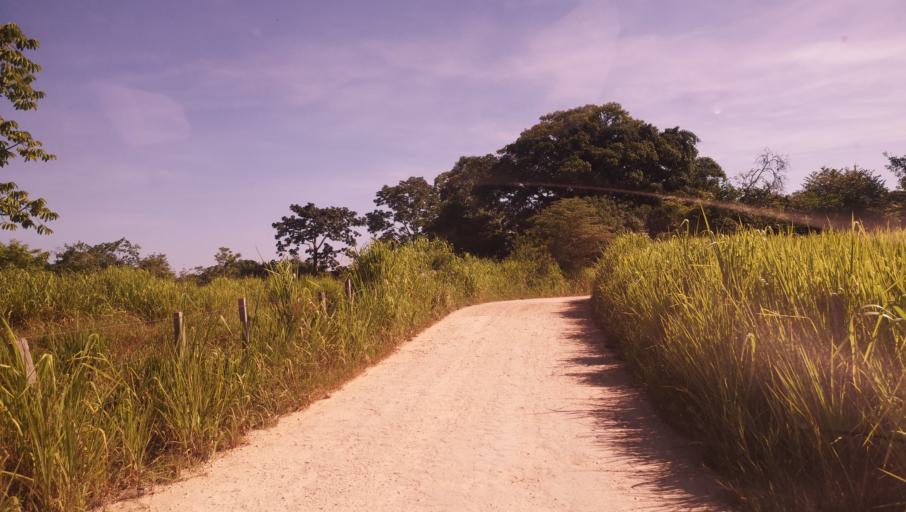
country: GT
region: Peten
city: Dolores
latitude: 16.7227
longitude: -89.3583
